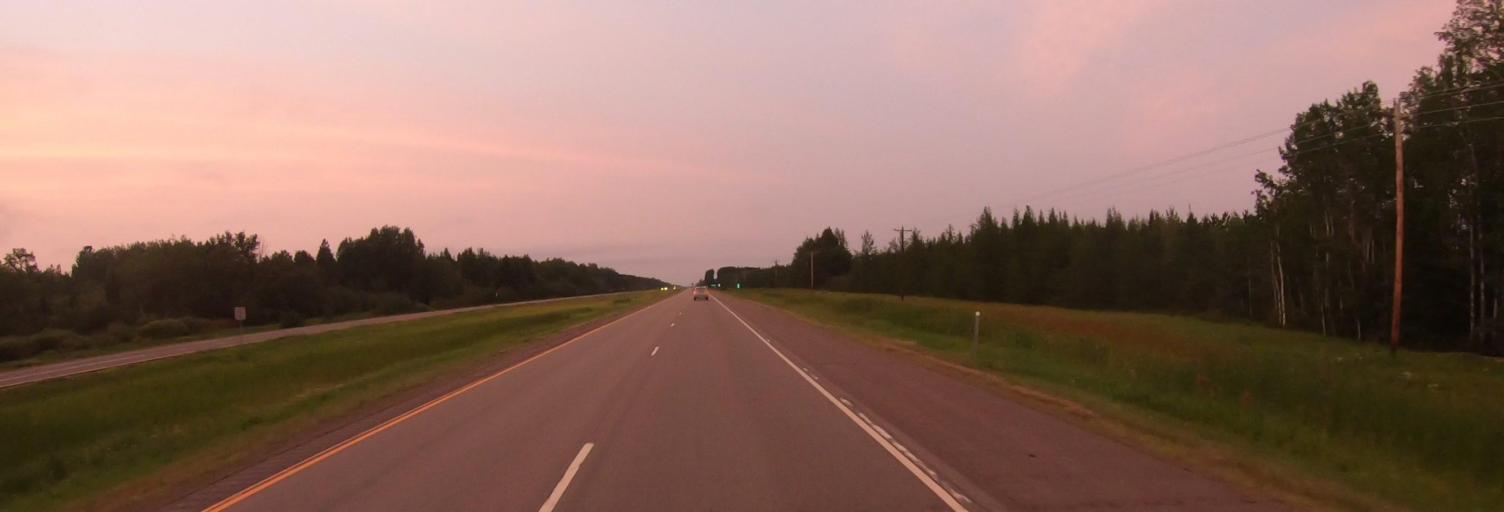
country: US
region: Minnesota
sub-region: Carlton County
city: Cloquet
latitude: 47.0818
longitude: -92.4715
